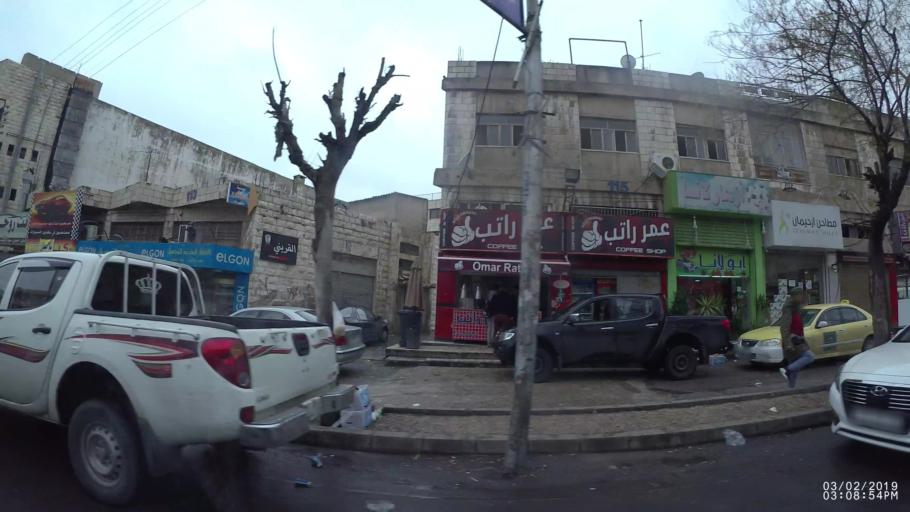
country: JO
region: Amman
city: Amman
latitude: 31.9640
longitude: 35.9227
